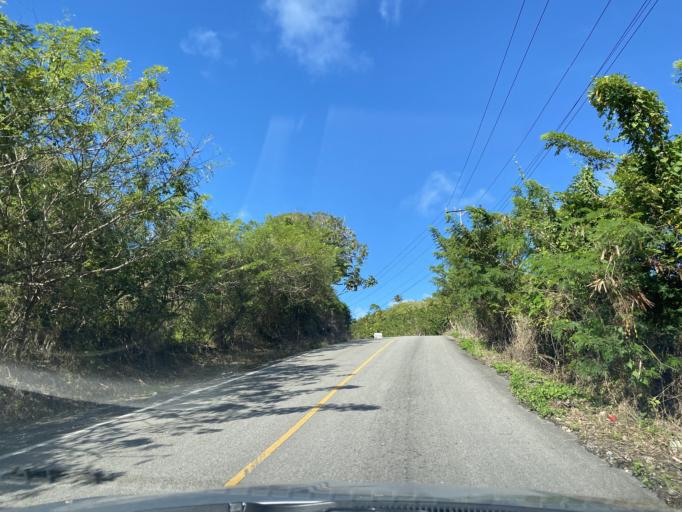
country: DO
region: Samana
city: Sanchez
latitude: 19.2448
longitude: -69.5958
